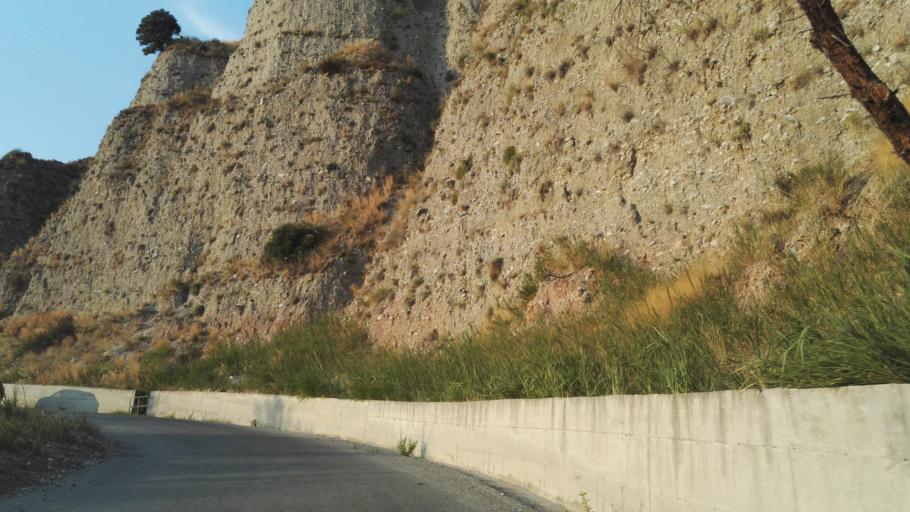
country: IT
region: Calabria
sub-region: Provincia di Reggio Calabria
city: Placanica
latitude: 38.3998
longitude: 16.4290
